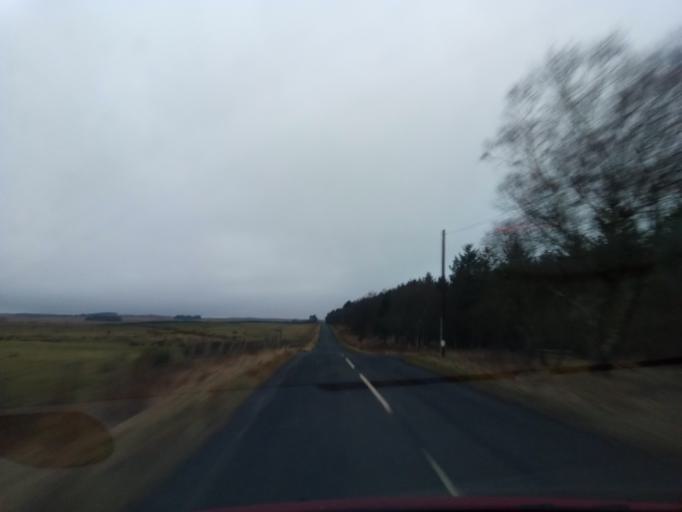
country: GB
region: England
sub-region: Northumberland
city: Rothley
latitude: 55.2013
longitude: -1.9903
